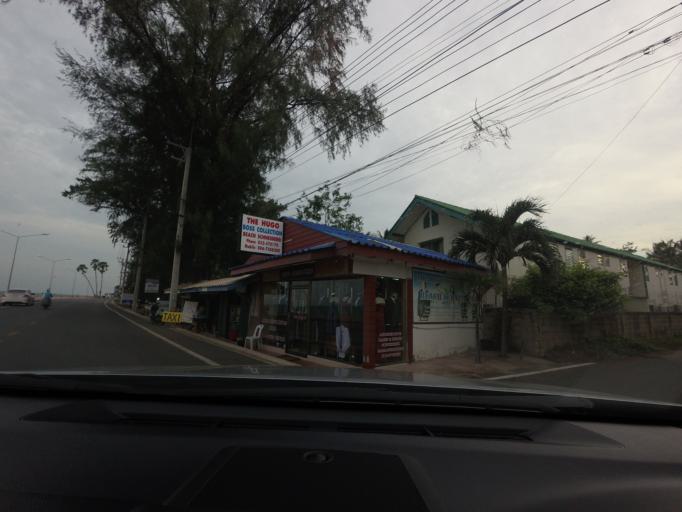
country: TH
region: Prachuap Khiri Khan
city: Pran Buri
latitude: 12.3839
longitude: 99.9993
